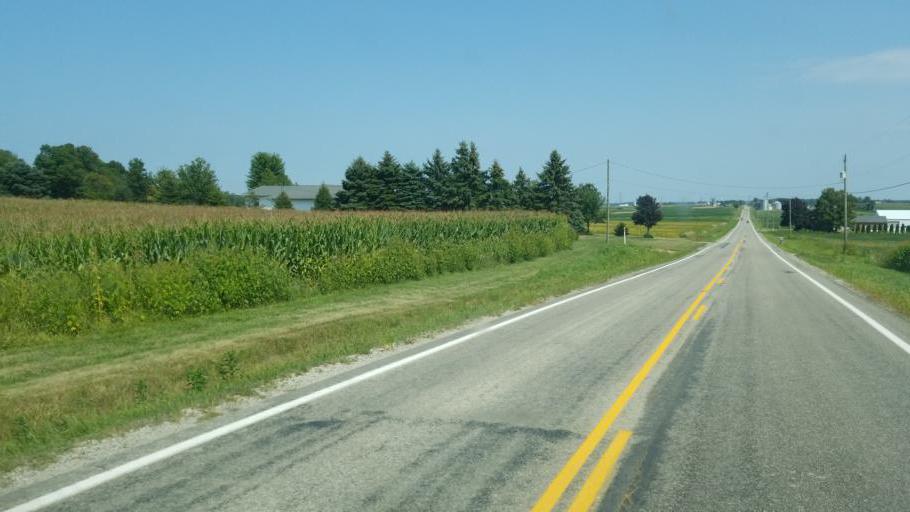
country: US
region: Ohio
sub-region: Richland County
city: Shelby
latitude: 40.8849
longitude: -82.7542
